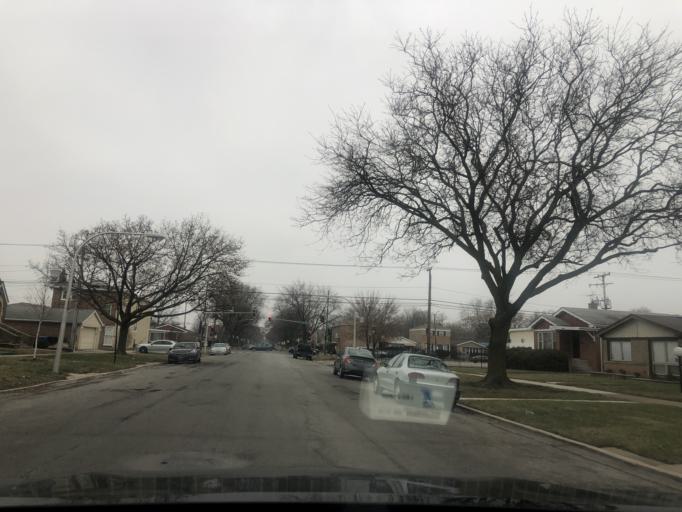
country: US
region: Illinois
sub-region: Cook County
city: Evergreen Park
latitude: 41.7375
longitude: -87.6194
